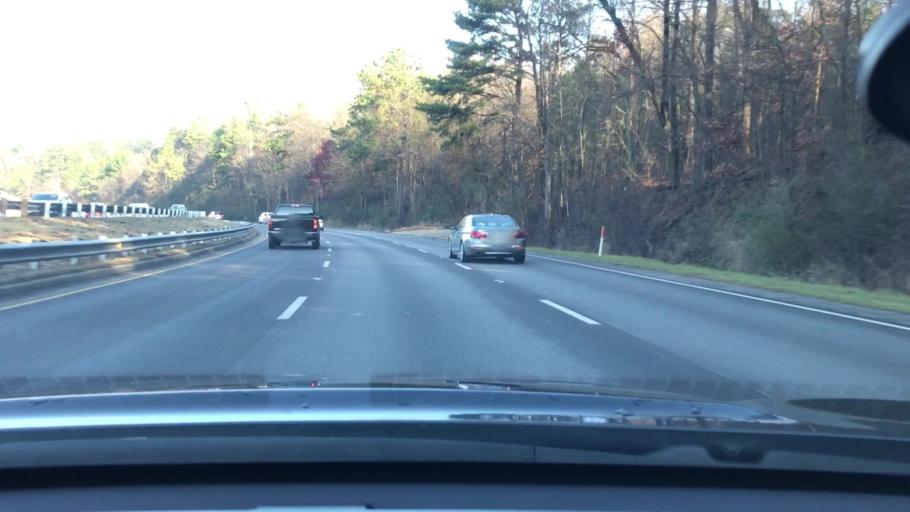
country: US
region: Alabama
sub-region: Jefferson County
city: Cahaba Heights
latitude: 33.4672
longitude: -86.7572
